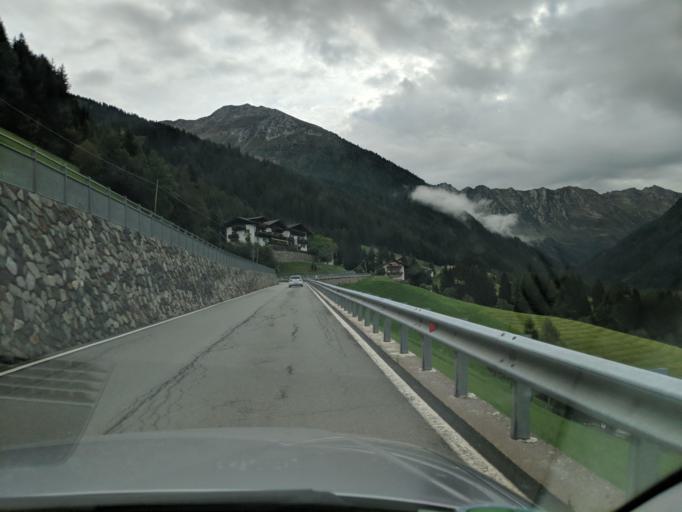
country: IT
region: Trentino-Alto Adige
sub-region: Bolzano
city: Racines
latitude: 46.8269
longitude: 11.2995
